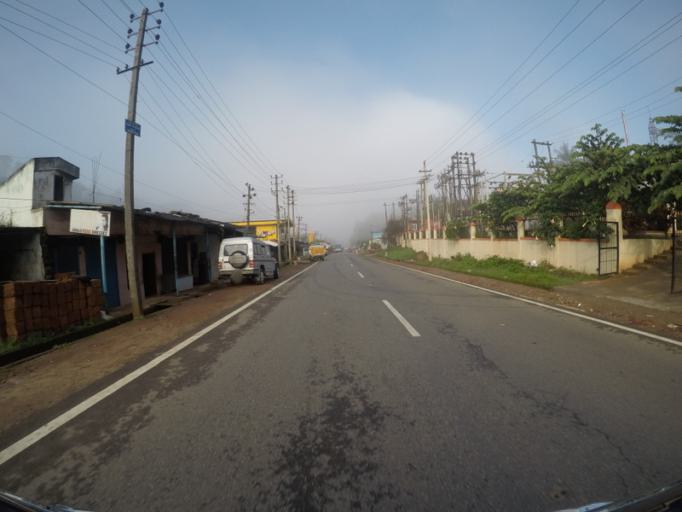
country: IN
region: Karnataka
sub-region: Kodagu
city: Suntikoppa
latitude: 12.4507
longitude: 75.8270
